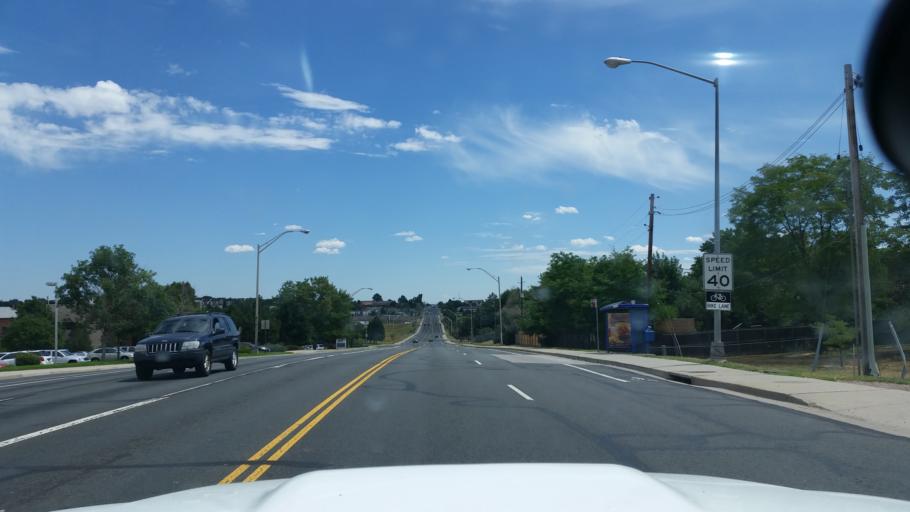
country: US
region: Colorado
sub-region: Adams County
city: Federal Heights
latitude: 39.8563
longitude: -104.9963
